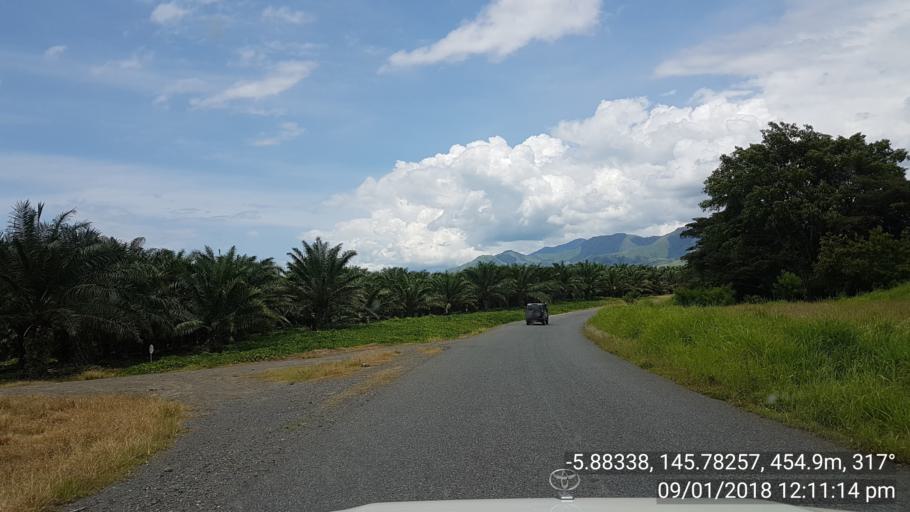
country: PG
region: Eastern Highlands
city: Kainantu
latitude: -5.8832
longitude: 145.7825
